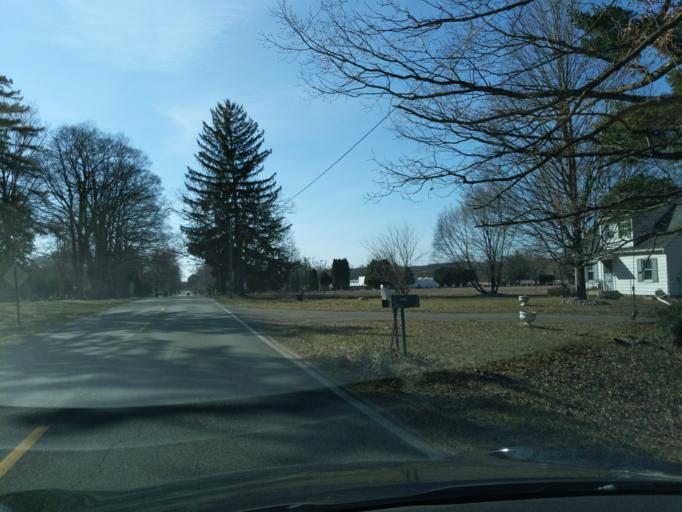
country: US
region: Michigan
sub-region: Ionia County
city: Saranac
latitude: 42.9299
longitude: -85.1972
